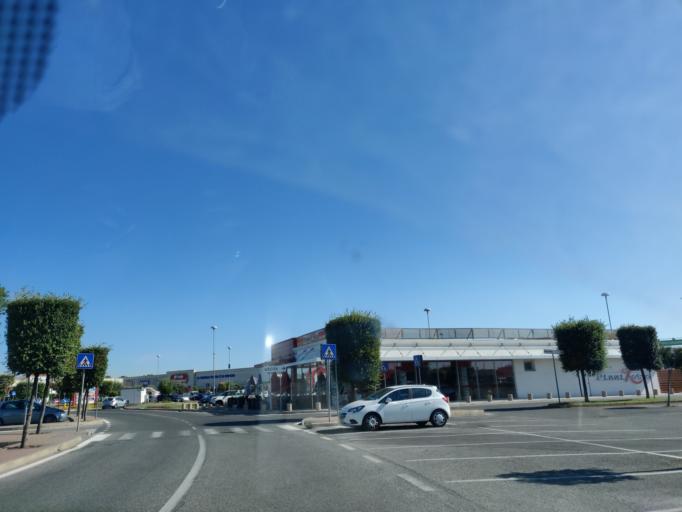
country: IT
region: Latium
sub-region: Citta metropolitana di Roma Capitale
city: Npp 23 (Parco Leonardo)
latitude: 41.8089
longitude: 12.3023
